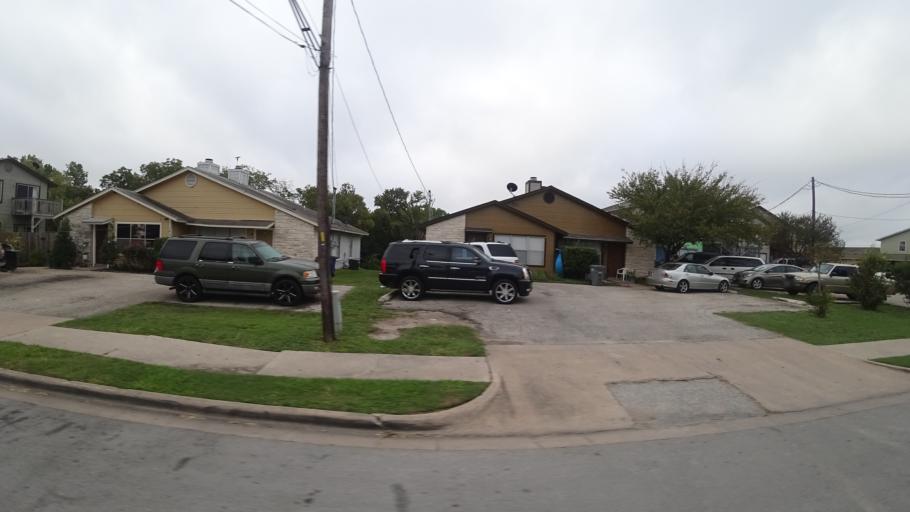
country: US
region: Texas
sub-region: Travis County
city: Wells Branch
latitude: 30.3500
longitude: -97.6902
